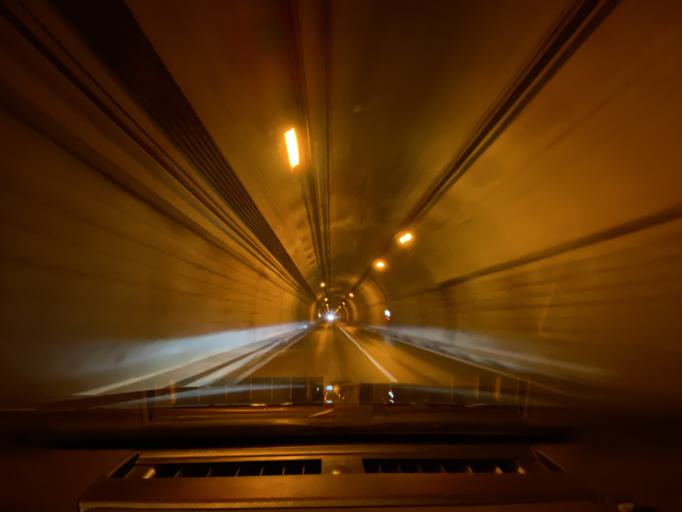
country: JP
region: Hokkaido
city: Rumoi
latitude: 43.7946
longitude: 141.3753
